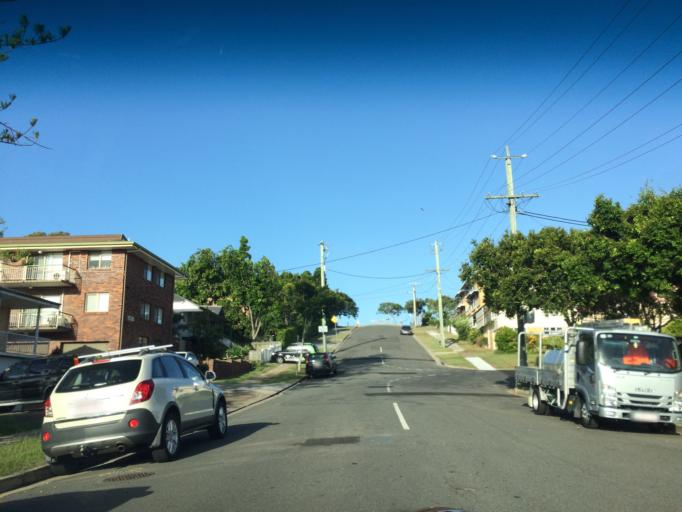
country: AU
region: Queensland
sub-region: Brisbane
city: Greenslopes
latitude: -27.4971
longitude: 153.0509
